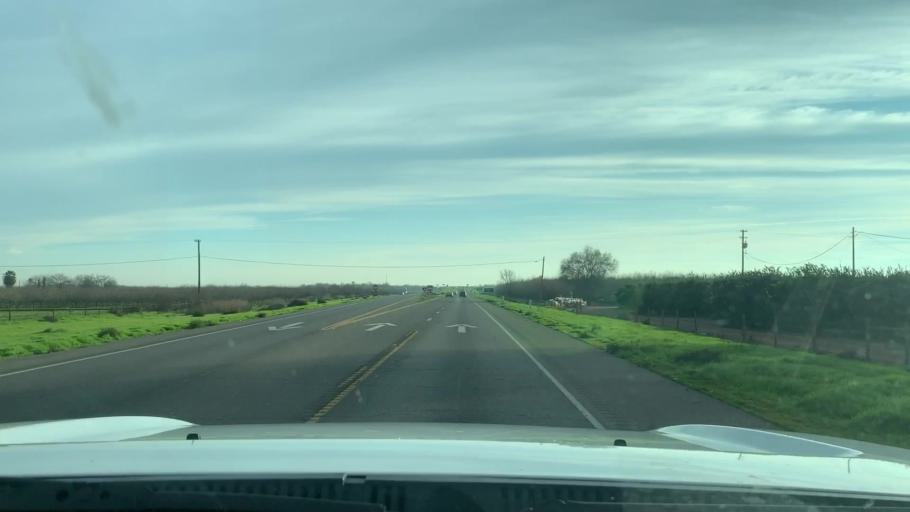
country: US
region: California
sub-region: Fresno County
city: Riverdale
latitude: 36.4103
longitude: -119.8055
